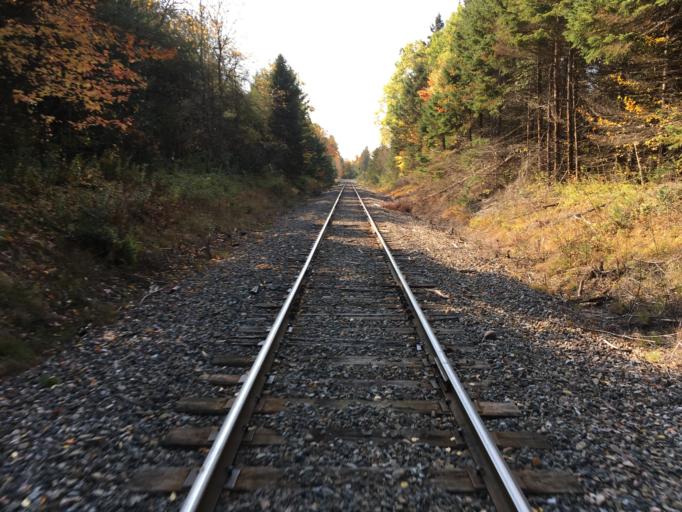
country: US
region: Vermont
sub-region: Caledonia County
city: Lyndonville
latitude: 44.6106
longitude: -71.9674
